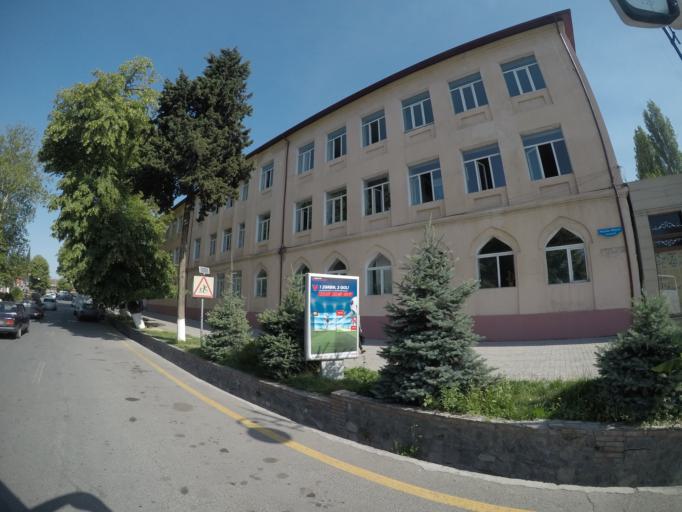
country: AZ
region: Shaki City
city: Sheki
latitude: 41.2035
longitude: 47.1808
